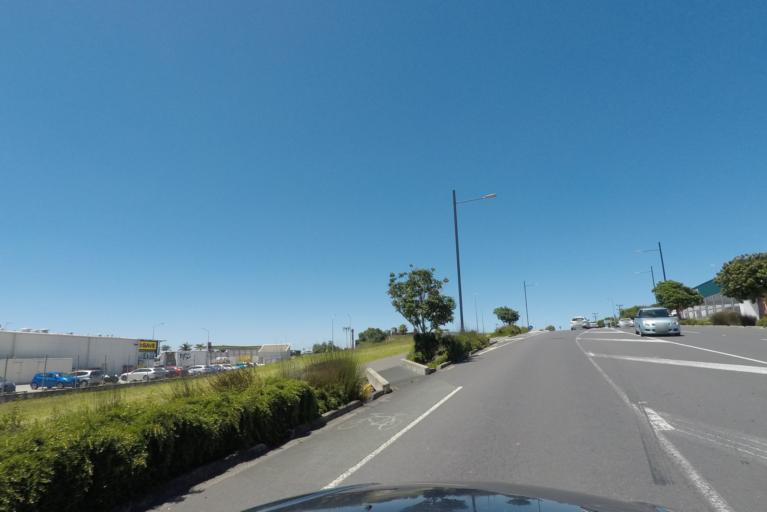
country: NZ
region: Auckland
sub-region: Auckland
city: Rosebank
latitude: -36.8204
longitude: 174.6073
